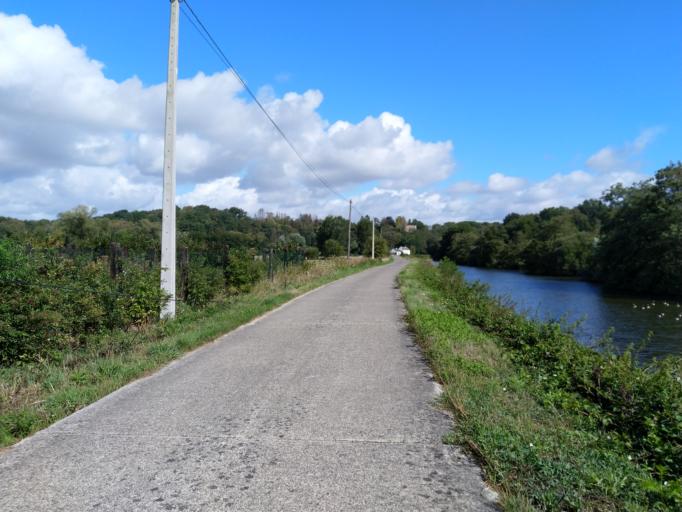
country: BE
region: Wallonia
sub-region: Province du Hainaut
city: Lobbes
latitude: 50.3289
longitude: 4.2303
